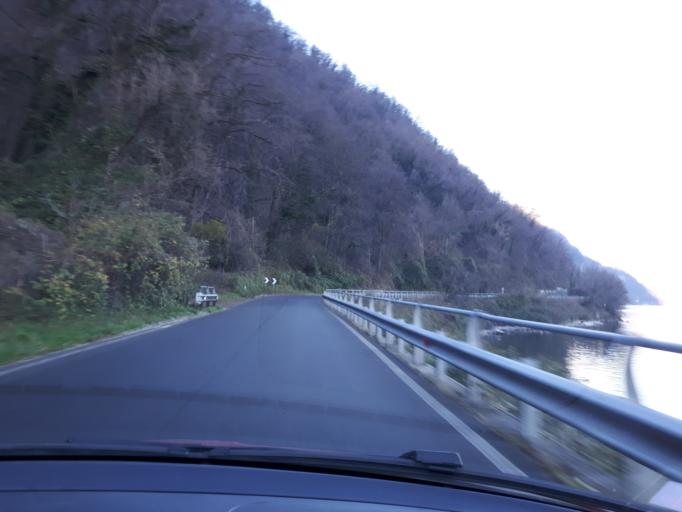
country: IT
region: Lombardy
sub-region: Provincia di Lecco
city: Abbadia Lariana
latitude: 45.8848
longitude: 9.3251
